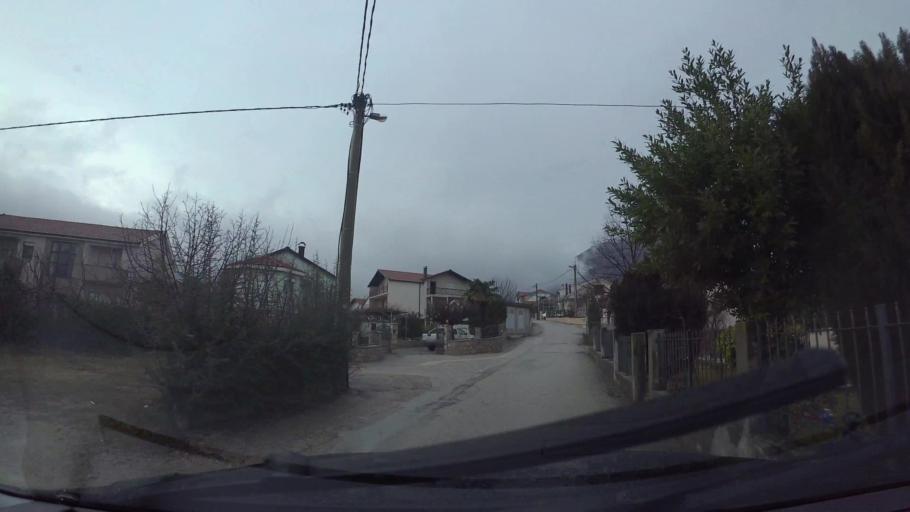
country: BA
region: Federation of Bosnia and Herzegovina
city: Cim
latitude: 43.3483
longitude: 17.7771
